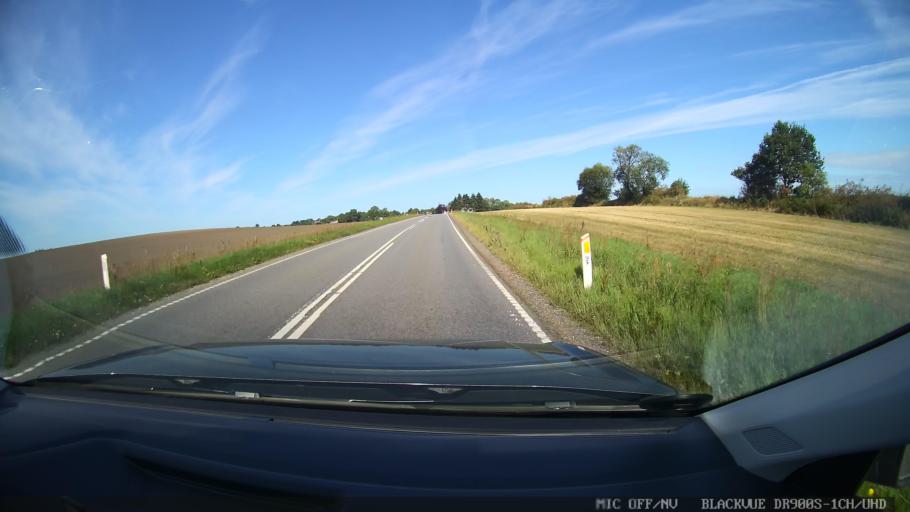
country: DK
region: North Denmark
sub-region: Mariagerfjord Kommune
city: Mariager
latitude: 56.6894
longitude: 9.9860
